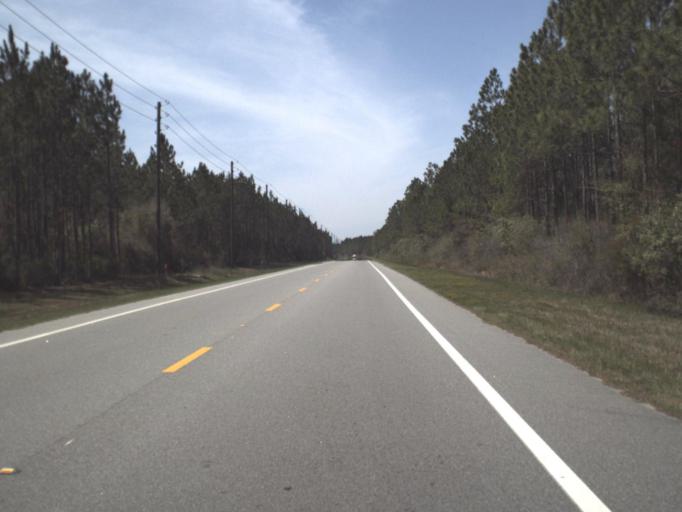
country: US
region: Florida
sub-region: Bay County
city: Lynn Haven
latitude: 30.3279
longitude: -85.7756
